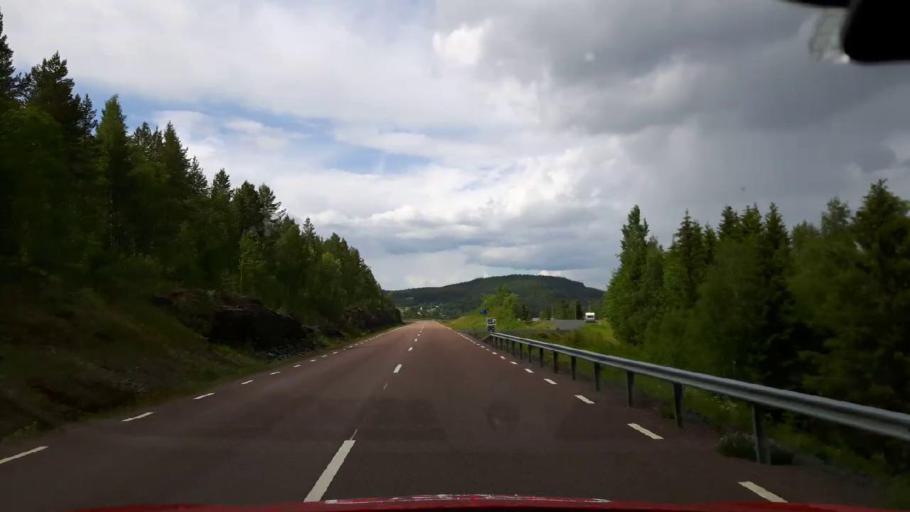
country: SE
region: Jaemtland
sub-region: Krokoms Kommun
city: Valla
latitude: 63.8971
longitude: 14.2510
